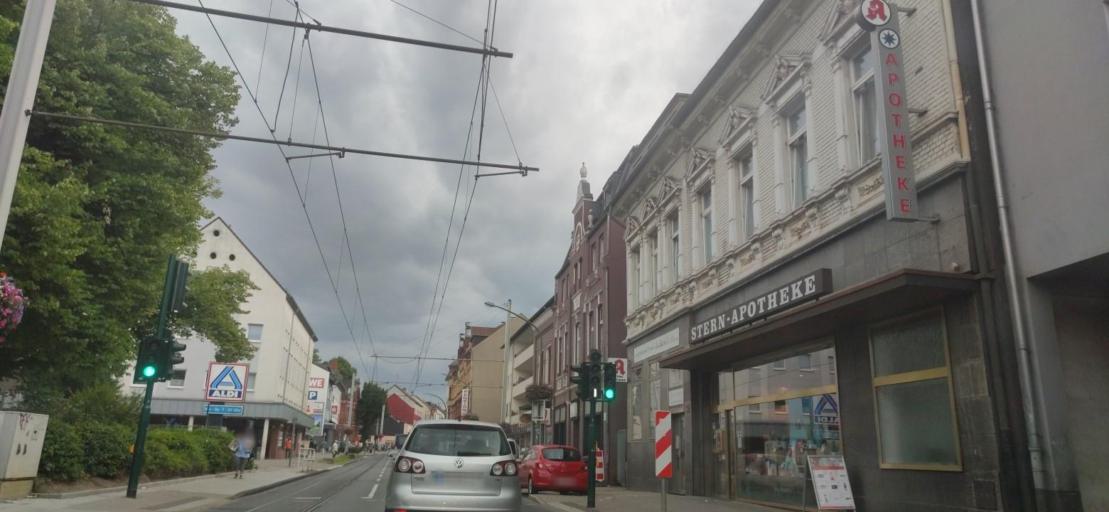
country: DE
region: North Rhine-Westphalia
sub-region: Regierungsbezirk Dusseldorf
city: Essen
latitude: 51.4988
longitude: 7.0484
